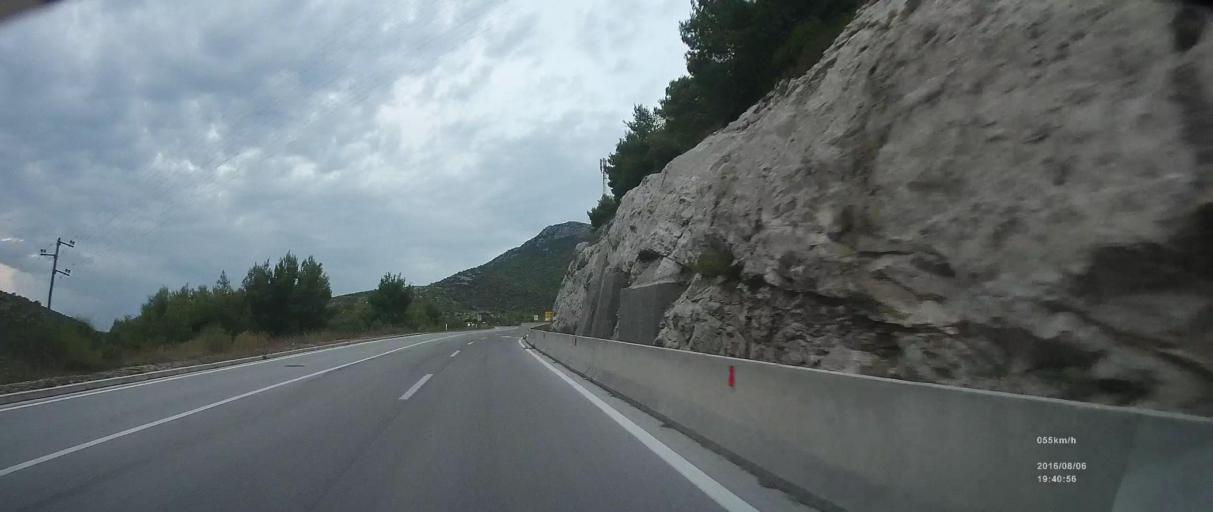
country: HR
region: Dubrovacko-Neretvanska
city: Ston
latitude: 42.8173
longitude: 17.6781
